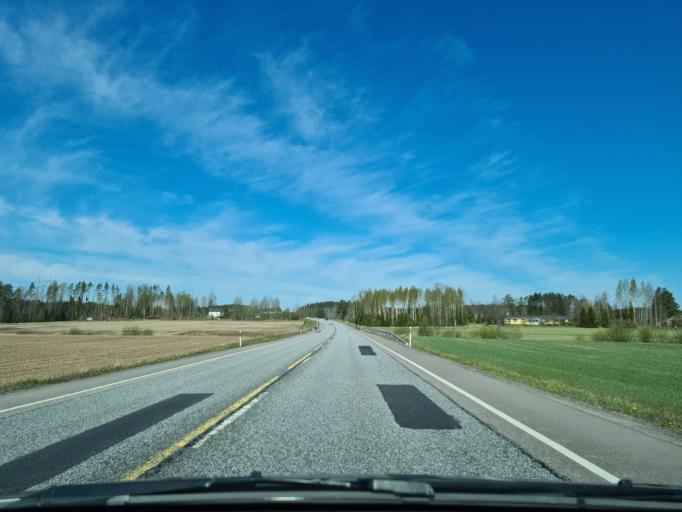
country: FI
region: Uusimaa
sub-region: Helsinki
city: Karkkila
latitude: 60.5624
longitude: 24.1907
